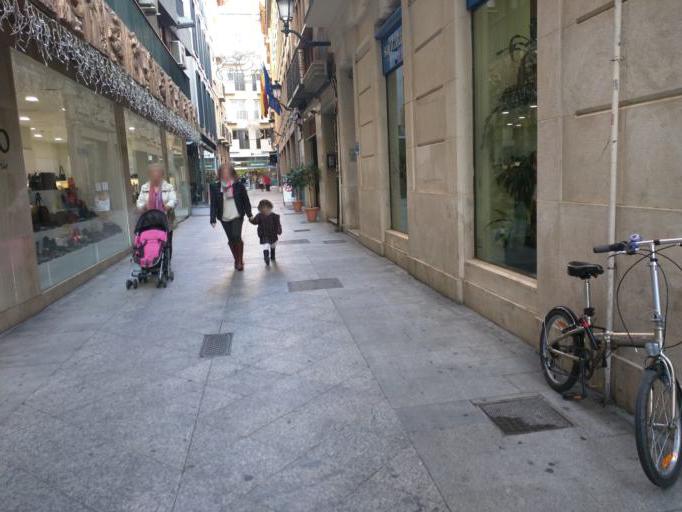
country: ES
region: Murcia
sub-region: Murcia
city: Murcia
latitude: 37.9860
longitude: -1.1295
